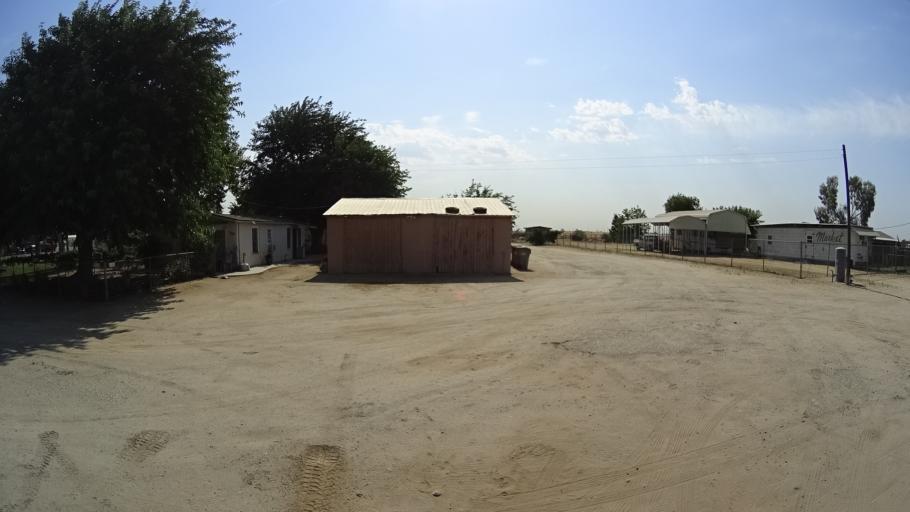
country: US
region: California
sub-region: Fresno County
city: West Park
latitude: 36.7407
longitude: -119.8533
